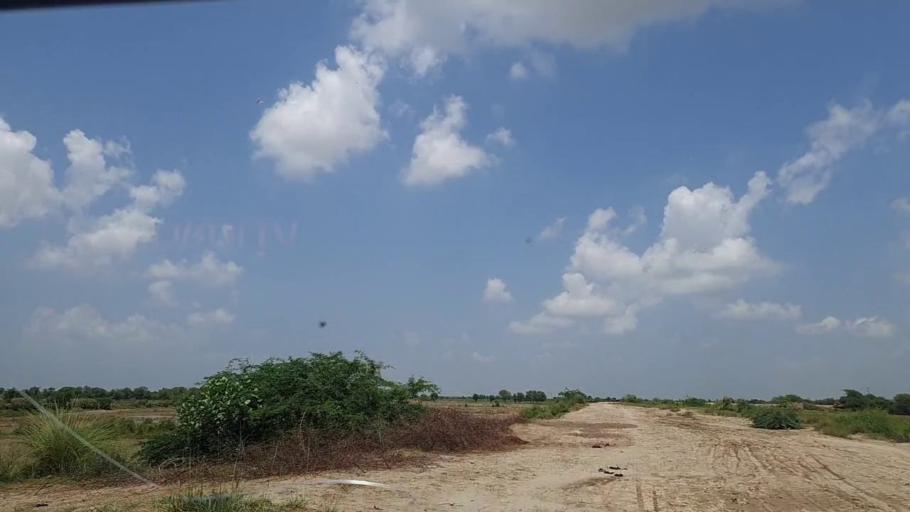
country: PK
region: Sindh
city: Tharu Shah
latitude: 26.9446
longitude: 68.0139
